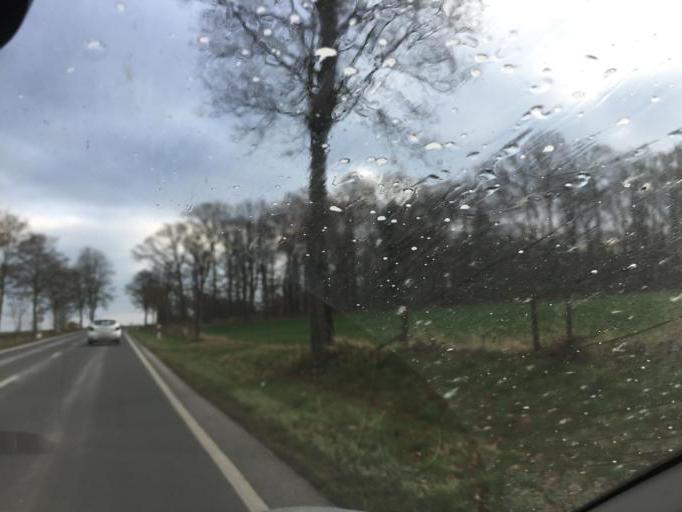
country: LU
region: Diekirch
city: Bettborn
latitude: 49.7705
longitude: 5.9254
